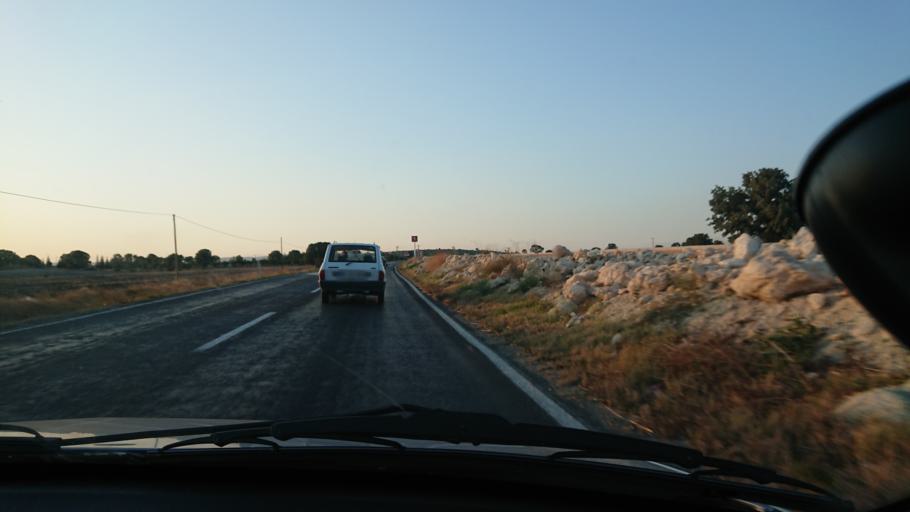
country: TR
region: Usak
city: Gure
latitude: 38.7218
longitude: 29.2034
